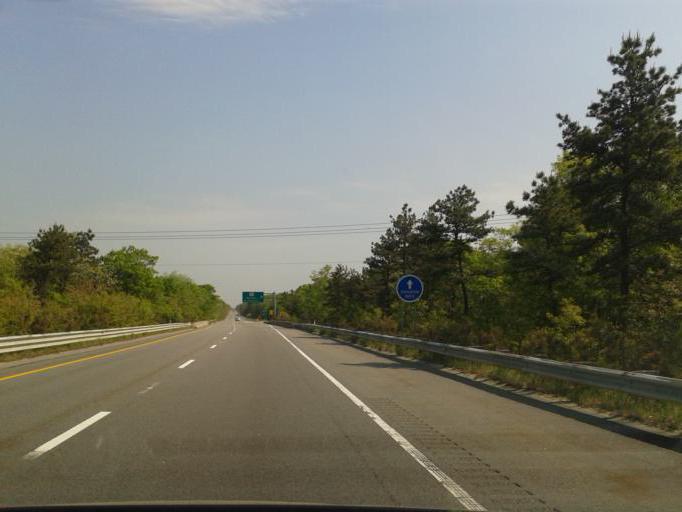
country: US
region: Massachusetts
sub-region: Barnstable County
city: North Falmouth
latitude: 41.6434
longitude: -70.6048
